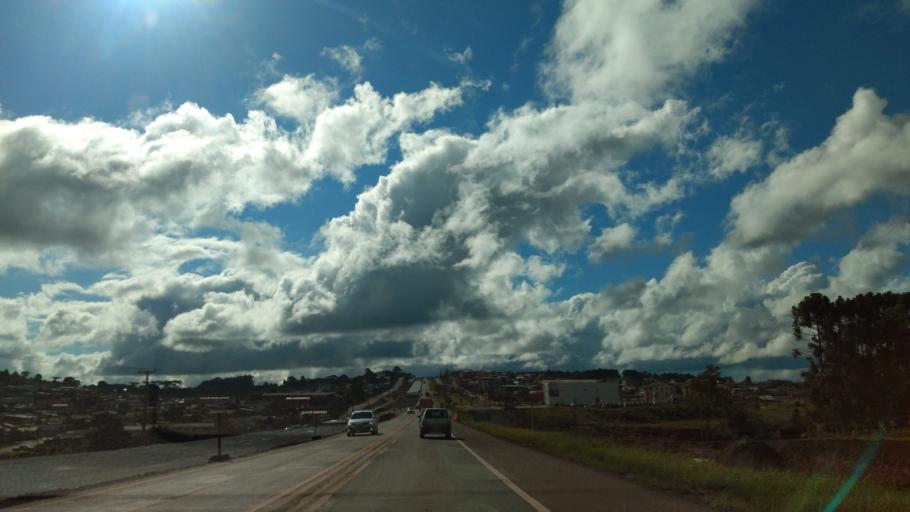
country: BR
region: Parana
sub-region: Guarapuava
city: Guarapuava
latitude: -25.3550
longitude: -51.4841
